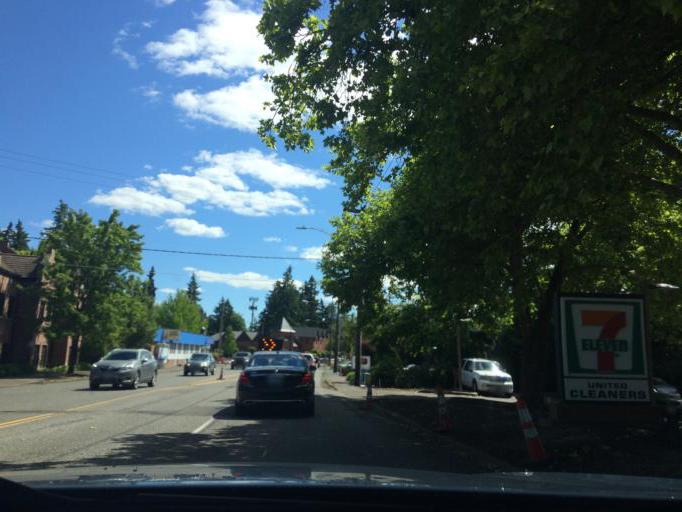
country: US
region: Oregon
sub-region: Washington County
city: Durham
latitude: 45.4139
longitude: -122.7169
